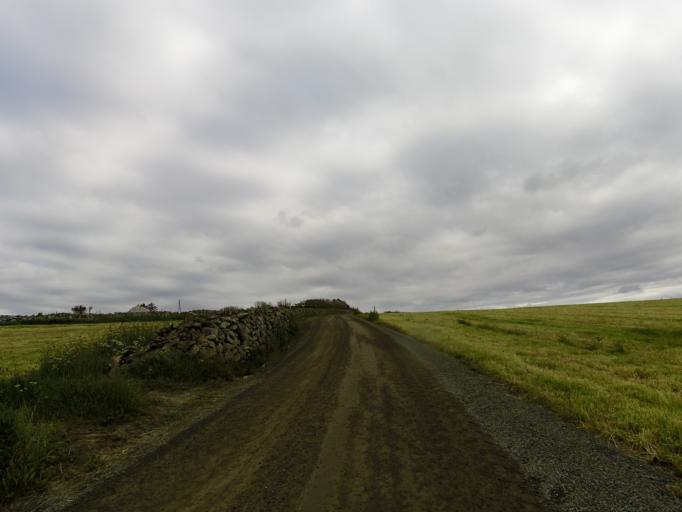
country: NO
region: Vest-Agder
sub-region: Farsund
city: Vestbygd
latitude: 58.1367
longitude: 6.6062
